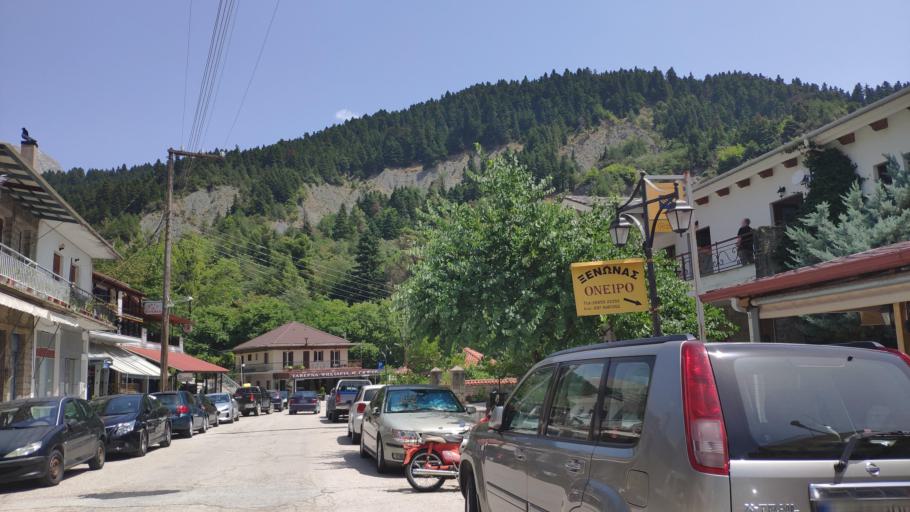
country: GR
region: Epirus
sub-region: Nomos Artas
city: Voulgareli
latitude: 39.3713
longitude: 21.1842
